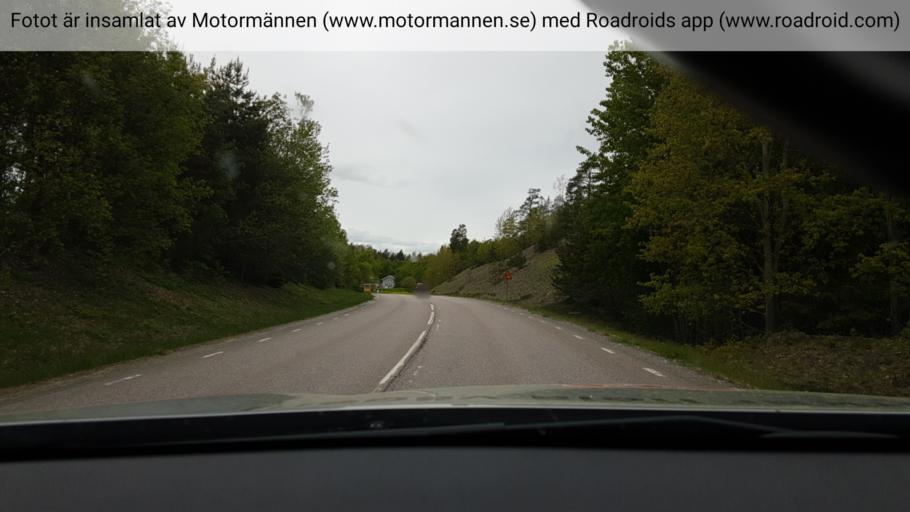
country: SE
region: Stockholm
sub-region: Vaxholms Kommun
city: Vaxholm
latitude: 59.3955
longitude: 18.4030
